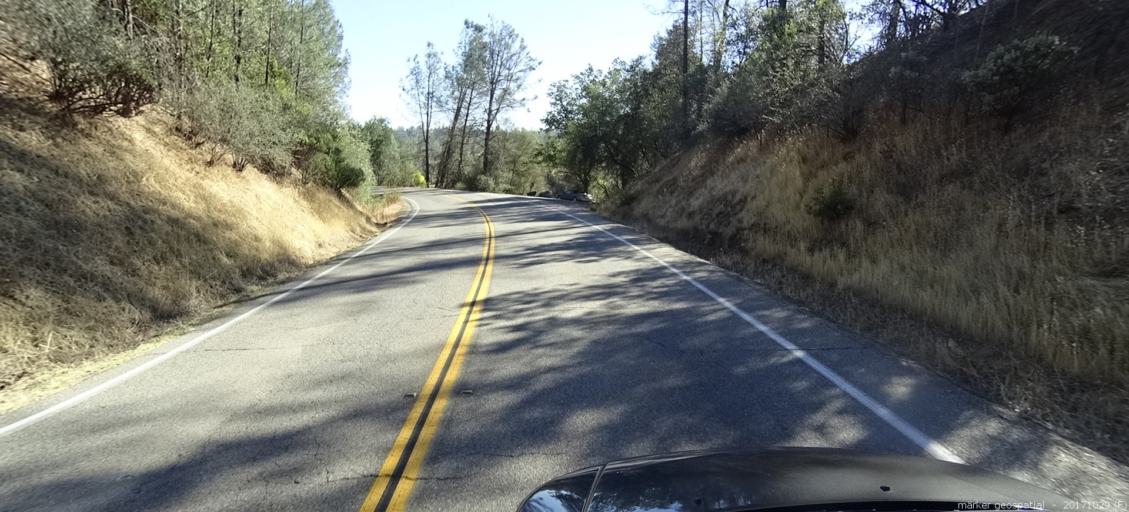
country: US
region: California
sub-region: Shasta County
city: Shasta
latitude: 40.4943
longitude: -122.4728
